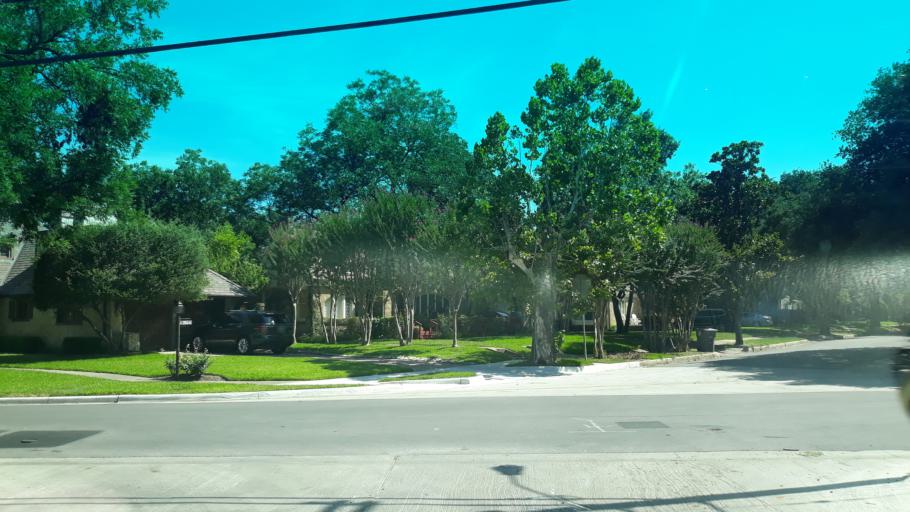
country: US
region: Texas
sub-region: Dallas County
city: Highland Park
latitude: 32.8212
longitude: -96.7499
